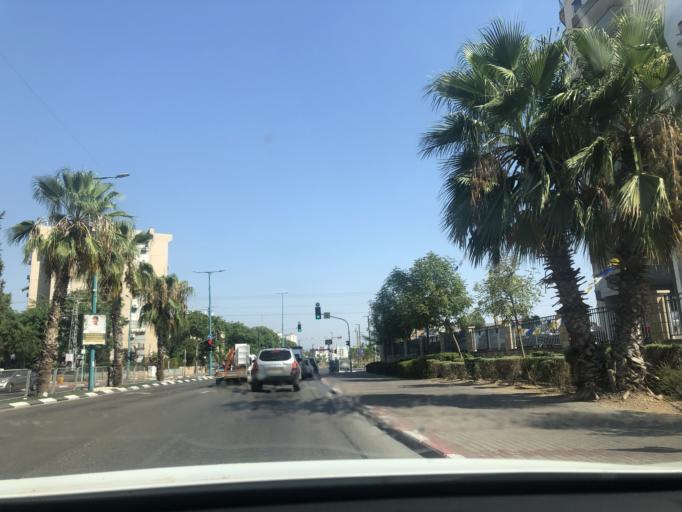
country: IL
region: Central District
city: Lod
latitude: 31.9454
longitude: 34.8934
